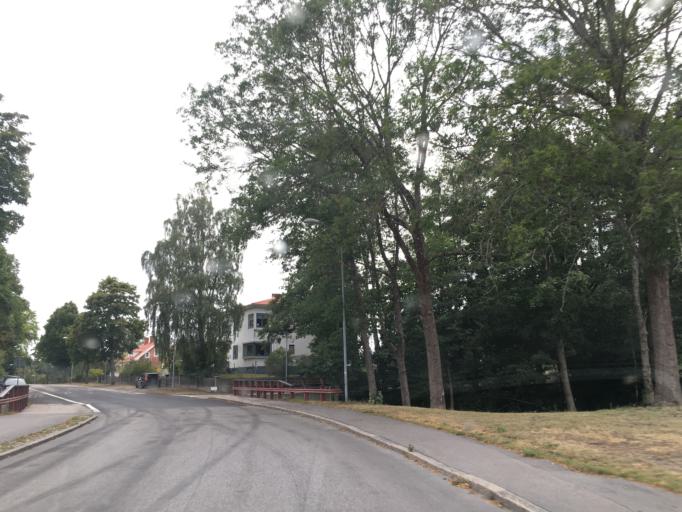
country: SE
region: Kalmar
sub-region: Nybro Kommun
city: Nybro
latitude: 56.7418
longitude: 15.9109
